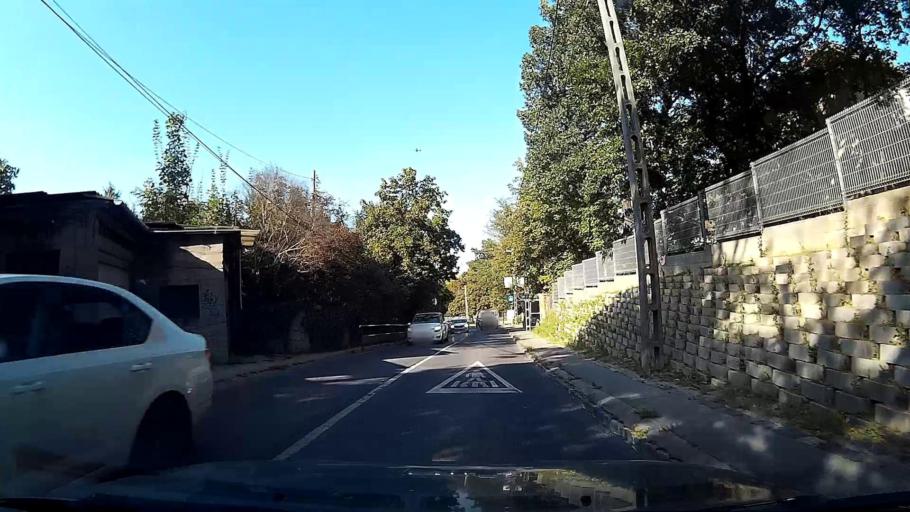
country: HU
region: Pest
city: Budaors
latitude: 47.4373
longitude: 18.9789
